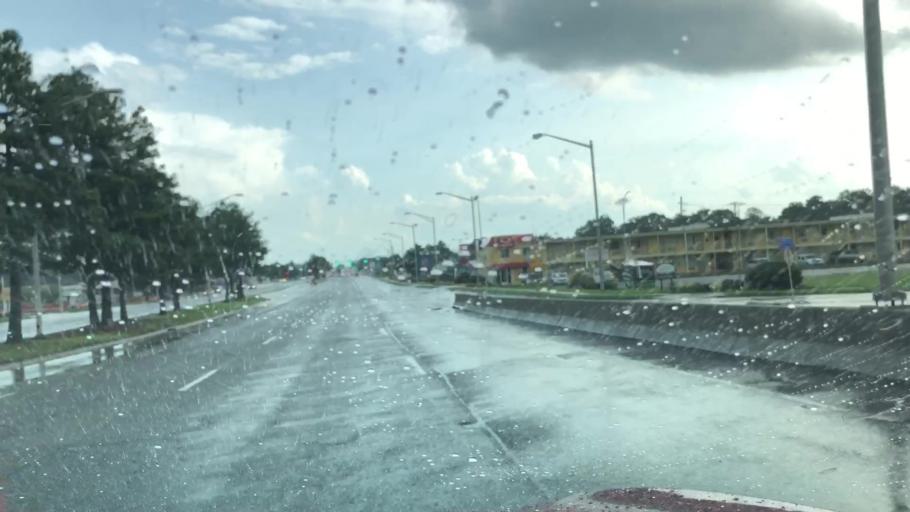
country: US
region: Virginia
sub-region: City of Chesapeake
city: Chesapeake
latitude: 36.8541
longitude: -76.2101
